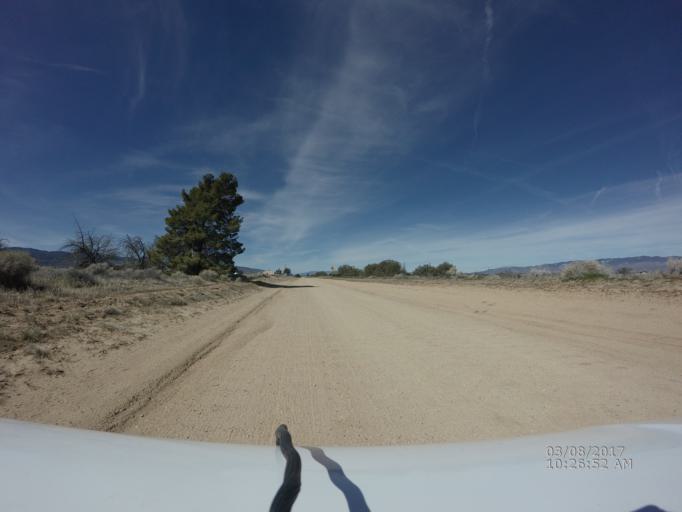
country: US
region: California
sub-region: Los Angeles County
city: Green Valley
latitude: 34.7601
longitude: -118.4640
